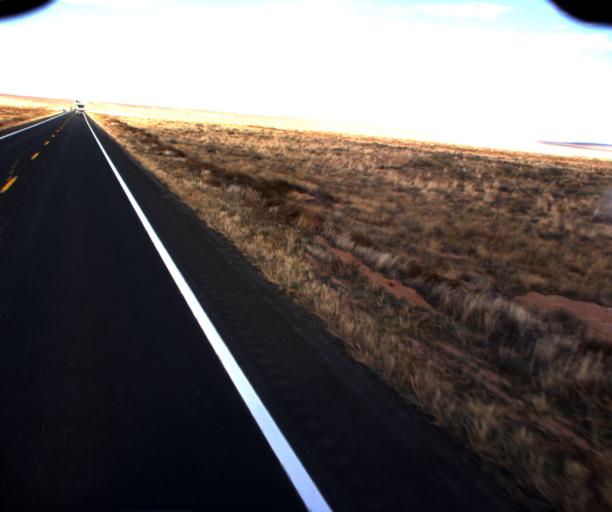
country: US
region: Arizona
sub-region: Apache County
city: Lukachukai
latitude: 36.9620
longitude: -109.4164
